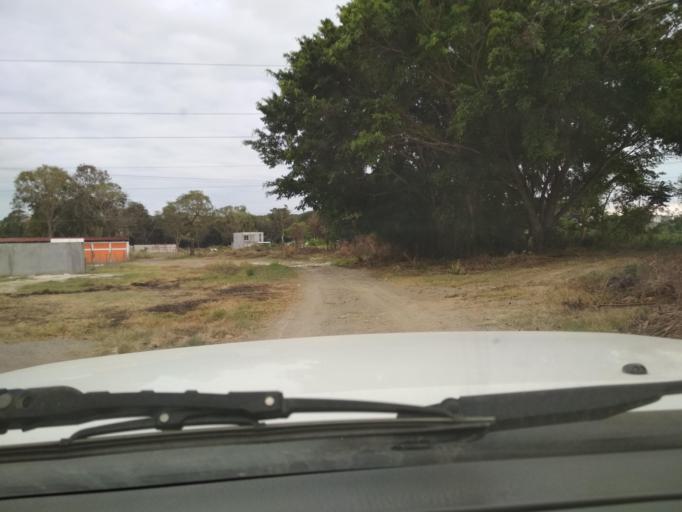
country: MX
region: Veracruz
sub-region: Medellin
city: Fraccionamiento Arboledas San Ramon
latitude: 19.0842
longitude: -96.1509
